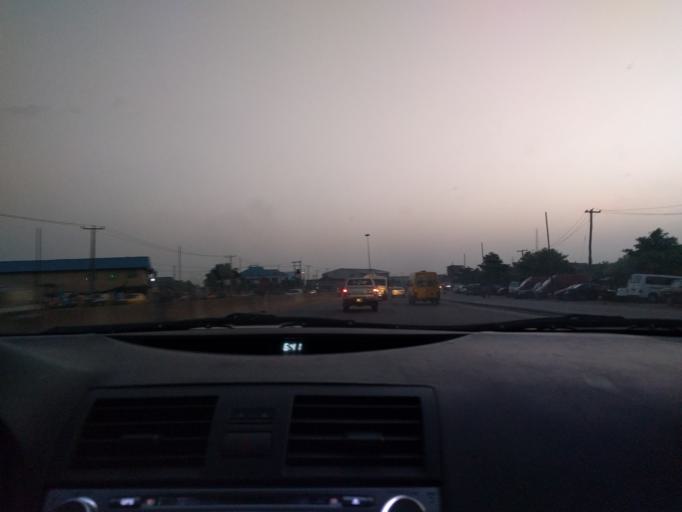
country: NG
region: Lagos
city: Mushin
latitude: 6.5175
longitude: 3.3345
